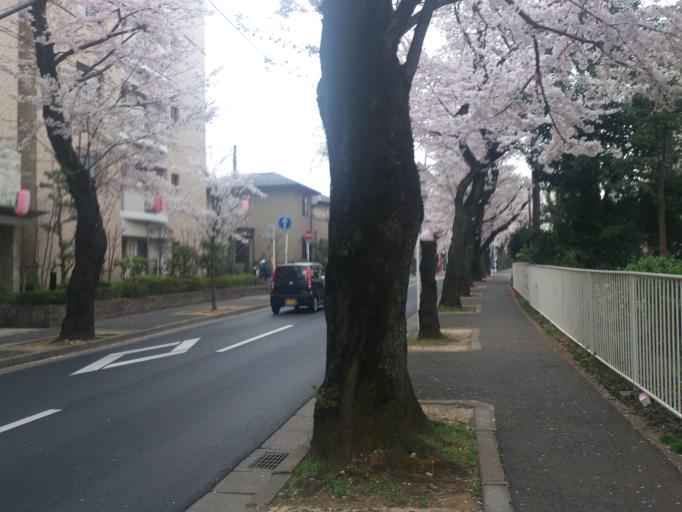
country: JP
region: Chiba
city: Kashiwa
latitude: 35.7999
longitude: 139.9625
